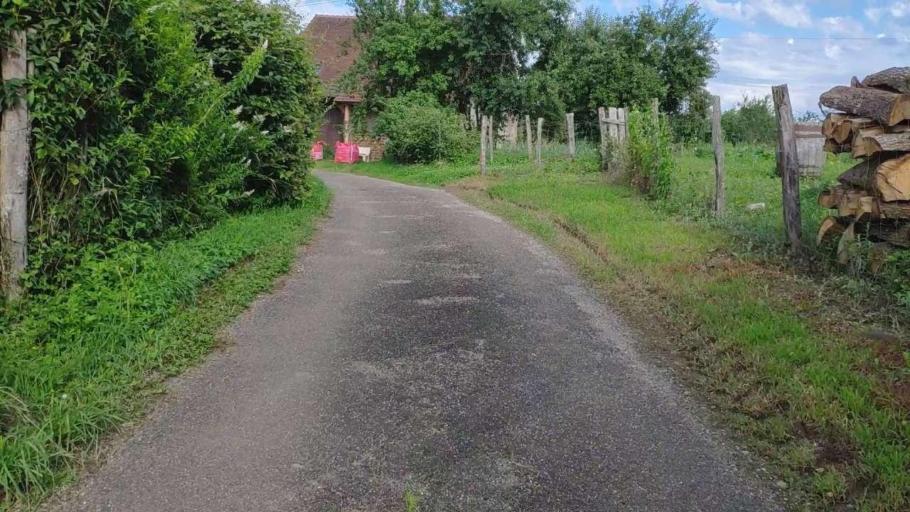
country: FR
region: Franche-Comte
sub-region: Departement du Jura
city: Bletterans
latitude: 46.8250
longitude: 5.5358
